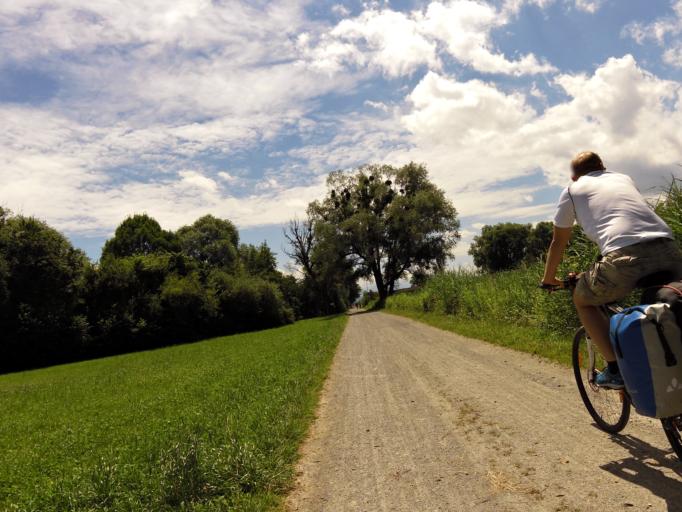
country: AT
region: Vorarlberg
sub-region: Politischer Bezirk Bregenz
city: Hard
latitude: 47.4902
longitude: 9.6756
